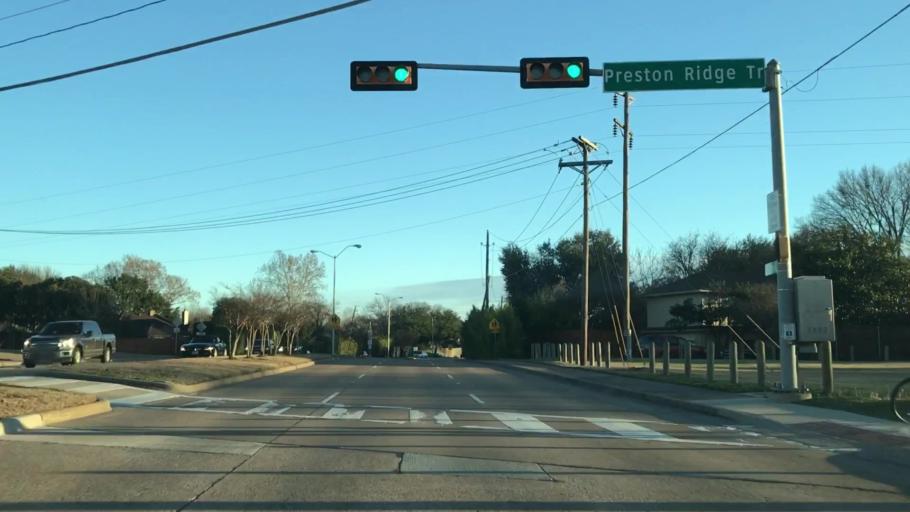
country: US
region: Texas
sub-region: Dallas County
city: Addison
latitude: 32.9765
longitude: -96.7850
